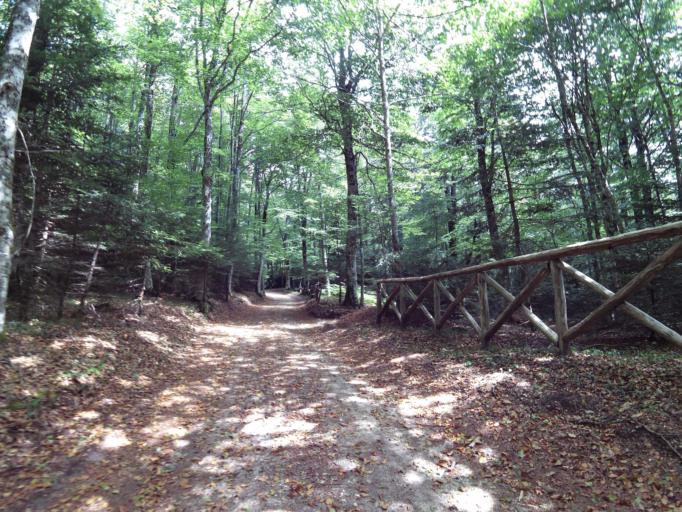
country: IT
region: Calabria
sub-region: Provincia di Vibo-Valentia
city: Mongiana
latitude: 38.5245
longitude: 16.3462
